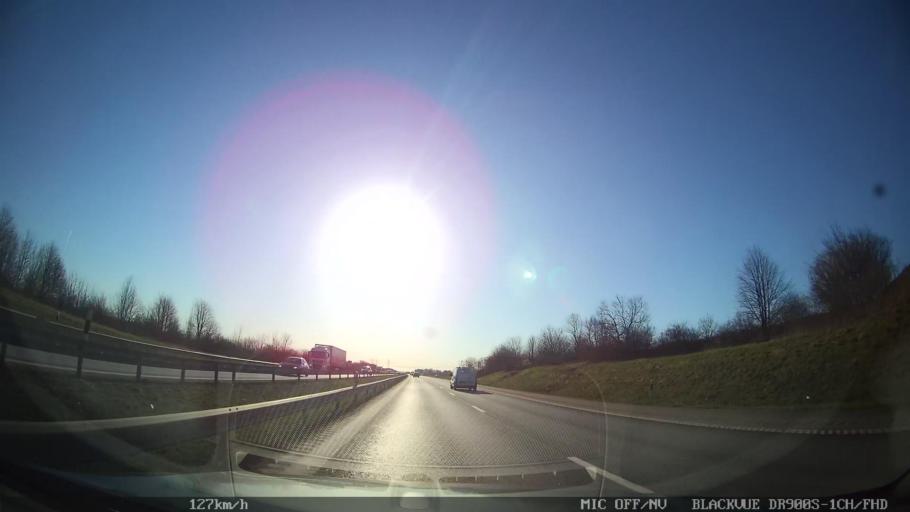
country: SE
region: Skane
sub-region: Kavlinge Kommun
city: Loddekopinge
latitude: 55.7451
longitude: 13.0294
